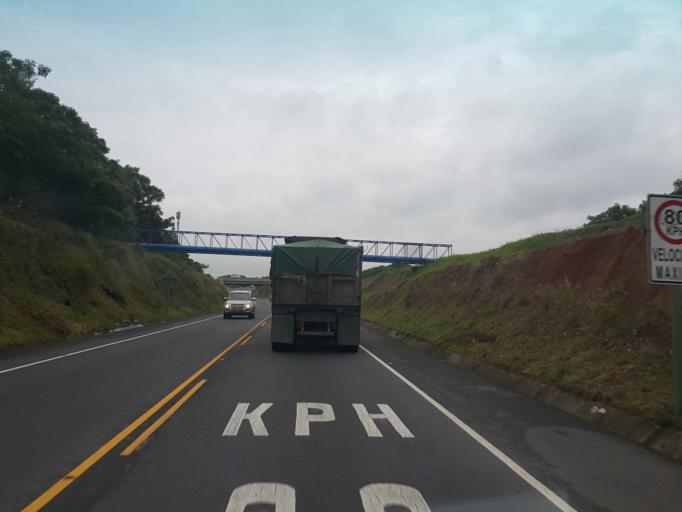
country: CR
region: Alajuela
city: Atenas
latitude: 9.9659
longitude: -84.3083
